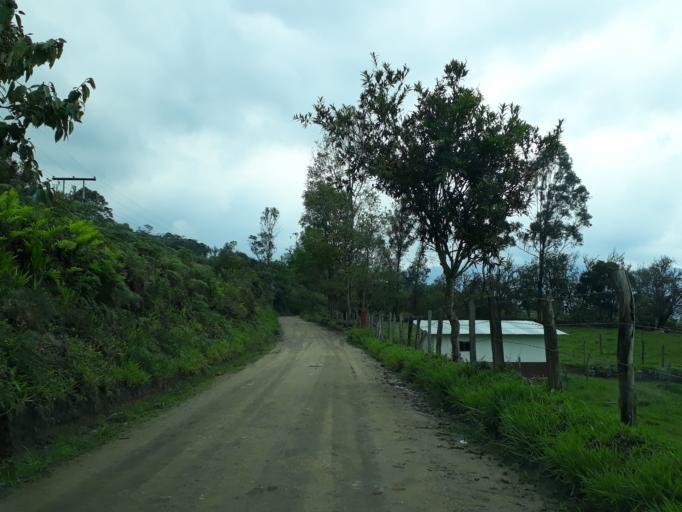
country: CO
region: Cundinamarca
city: Manta
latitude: 4.9940
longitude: -73.5555
